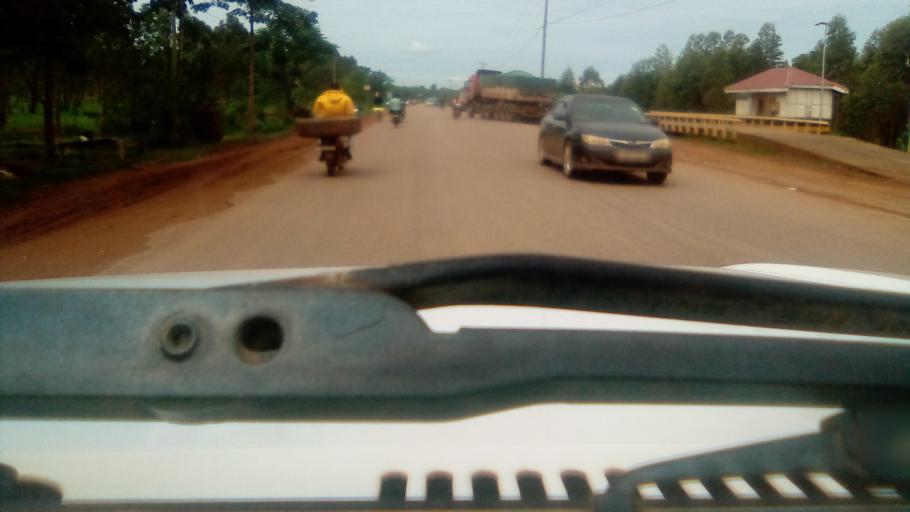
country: UG
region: Eastern Region
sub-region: Mbale District
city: Mbale
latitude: 1.0597
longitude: 34.1805
